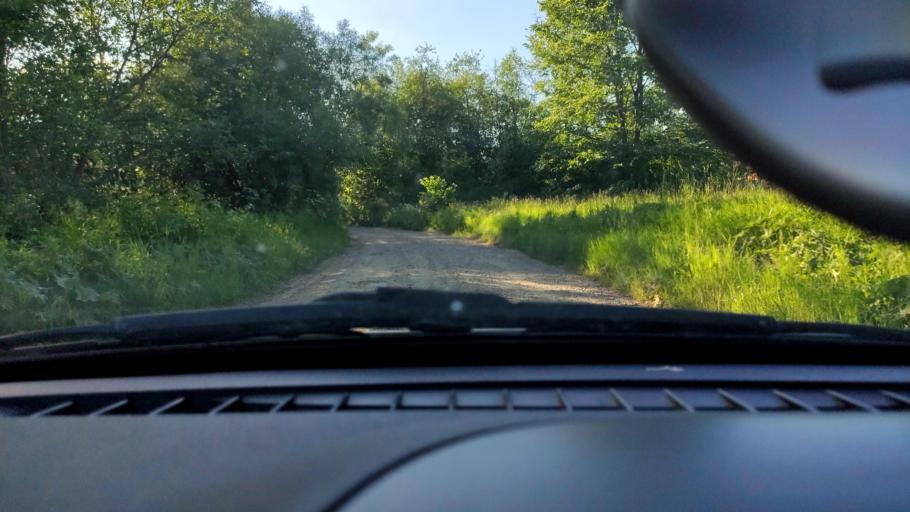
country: RU
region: Perm
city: Bershet'
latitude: 57.6978
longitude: 56.4148
